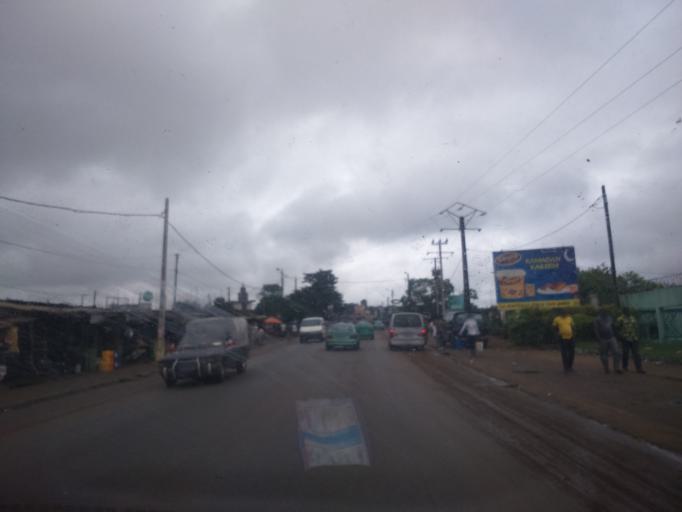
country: CI
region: Sud-Comoe
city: Bonoua
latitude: 5.2680
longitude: -3.5979
